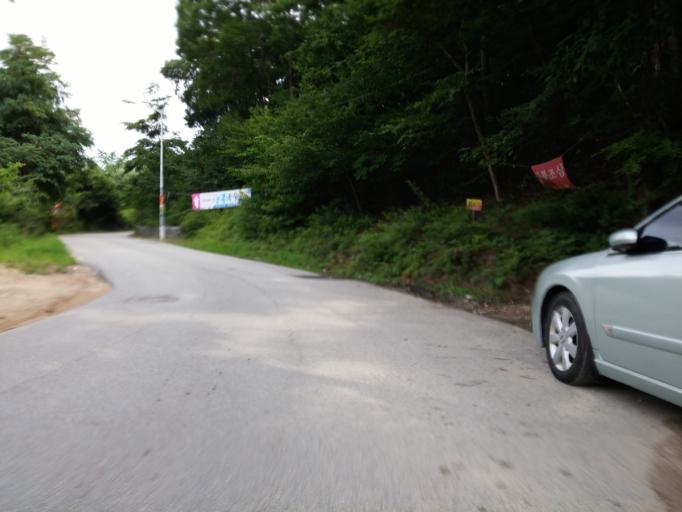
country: KR
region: Daejeon
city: Songgang-dong
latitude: 36.3682
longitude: 127.2596
